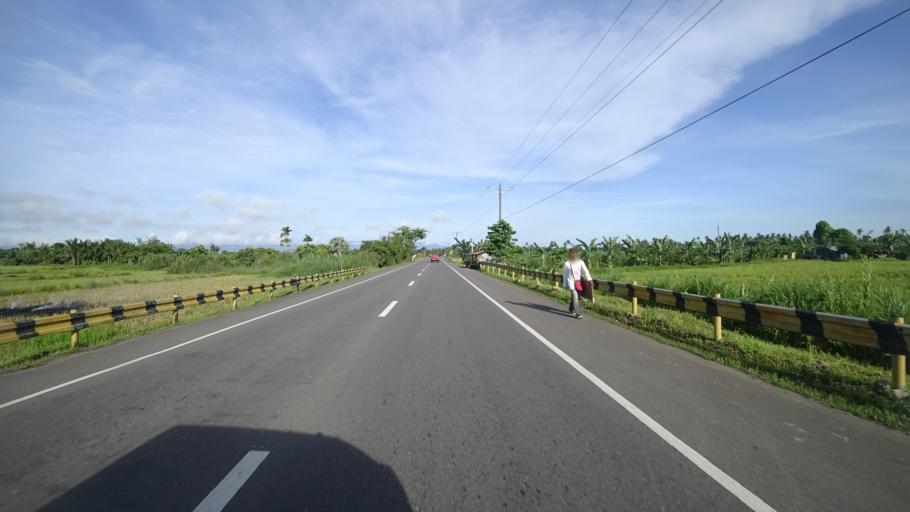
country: PH
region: Eastern Visayas
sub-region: Province of Leyte
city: Santa Fe
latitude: 11.1922
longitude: 124.8854
